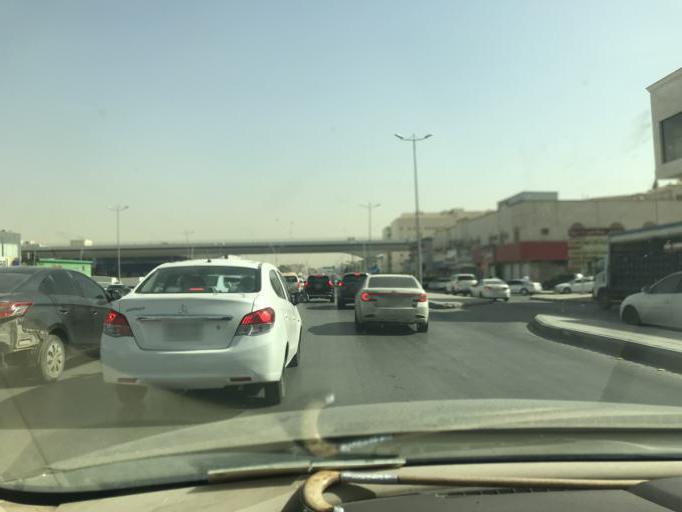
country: SA
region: Ar Riyad
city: Riyadh
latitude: 24.7943
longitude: 46.7431
